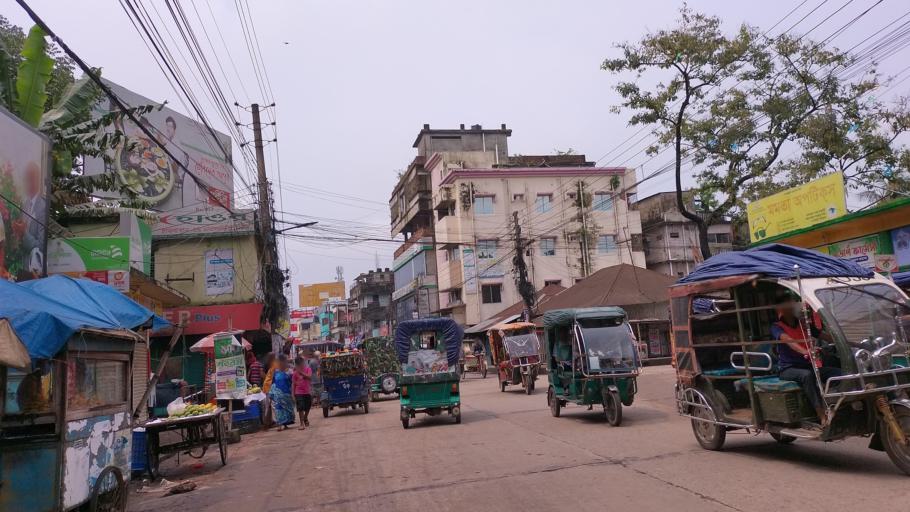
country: BD
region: Dhaka
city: Netrakona
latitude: 24.8807
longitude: 90.7318
